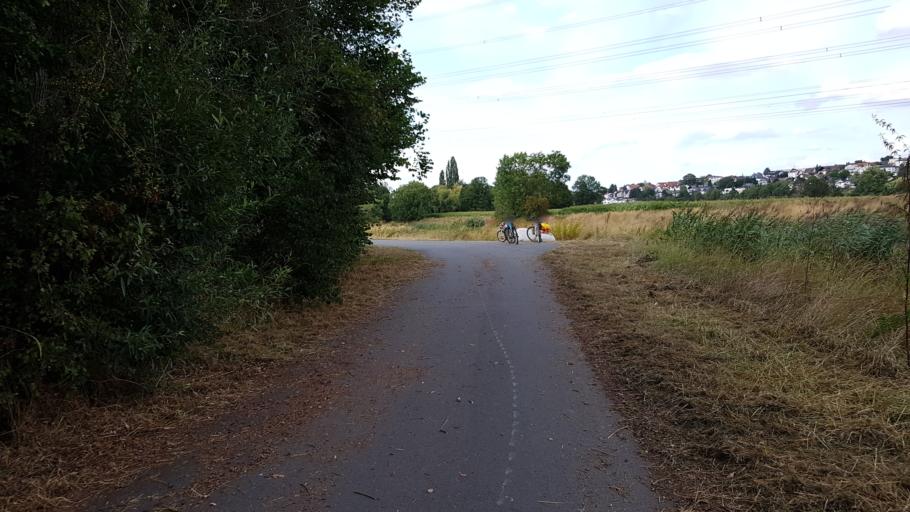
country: DE
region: Hesse
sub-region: Regierungsbezirk Darmstadt
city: Karben
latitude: 50.2131
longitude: 8.7725
